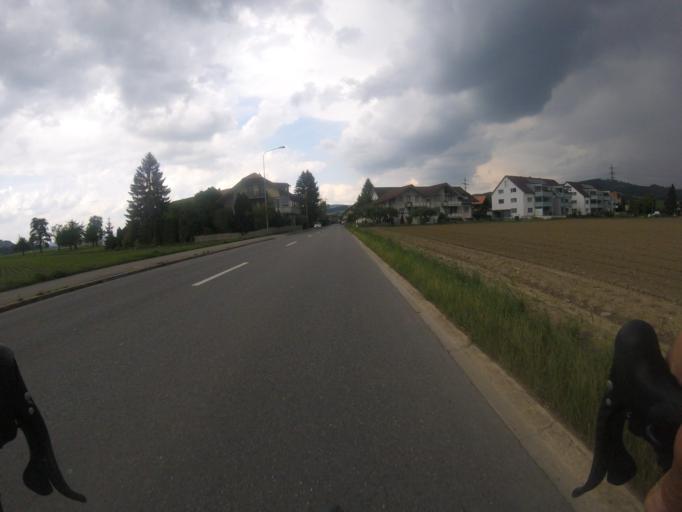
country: CH
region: Bern
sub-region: Bern-Mittelland District
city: Niederwichtrach
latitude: 46.8386
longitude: 7.5664
